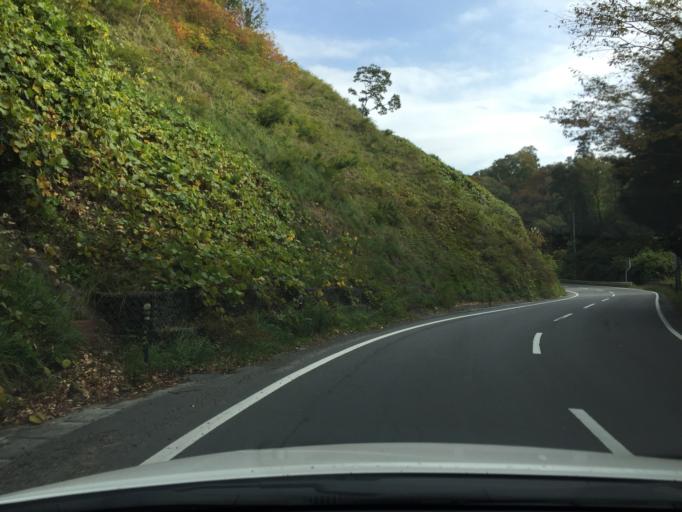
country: JP
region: Fukushima
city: Ishikawa
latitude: 36.9948
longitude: 140.4031
